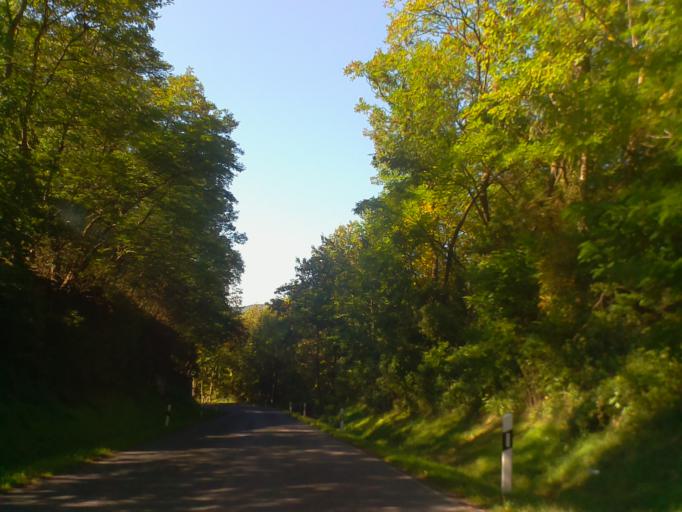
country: DE
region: Thuringia
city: Grosspurschutz
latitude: 50.8023
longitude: 11.5990
